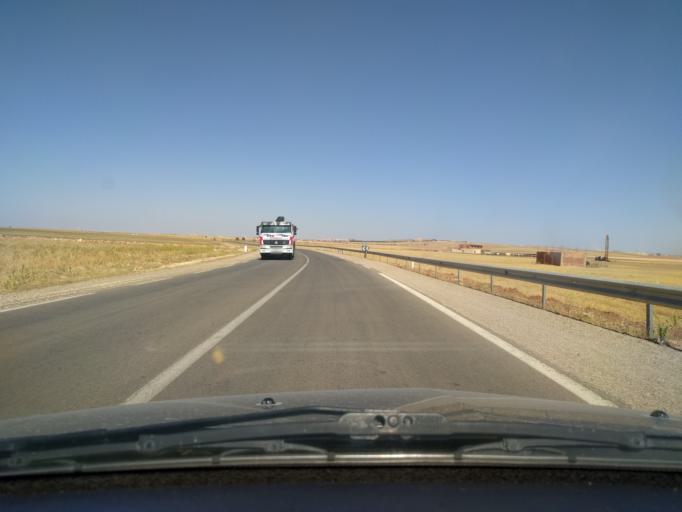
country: DZ
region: Tiaret
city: Frenda
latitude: 34.9050
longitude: 1.1453
